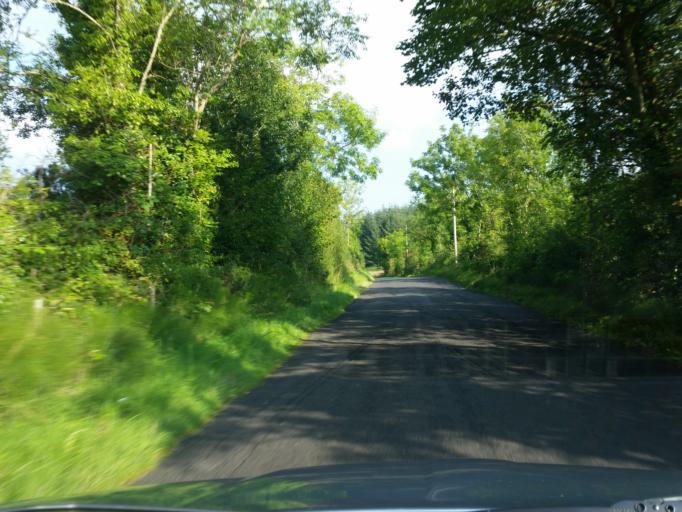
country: GB
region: Northern Ireland
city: Lisnaskea
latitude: 54.2801
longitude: -7.4095
